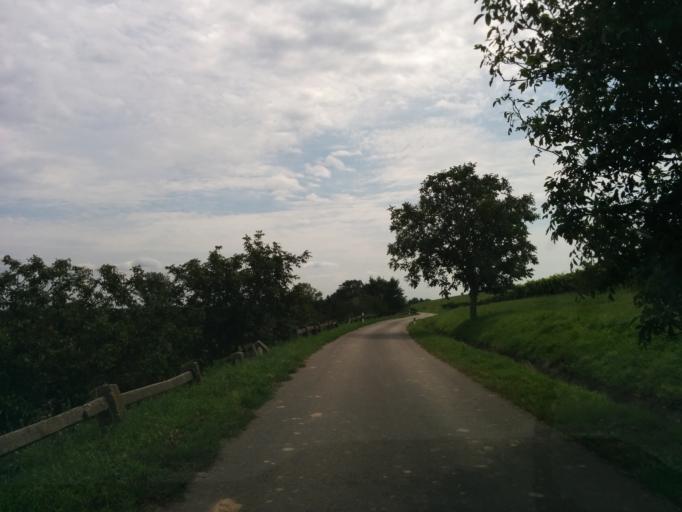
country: HU
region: Gyor-Moson-Sopron
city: Fertorakos
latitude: 47.6793
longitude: 16.6710
